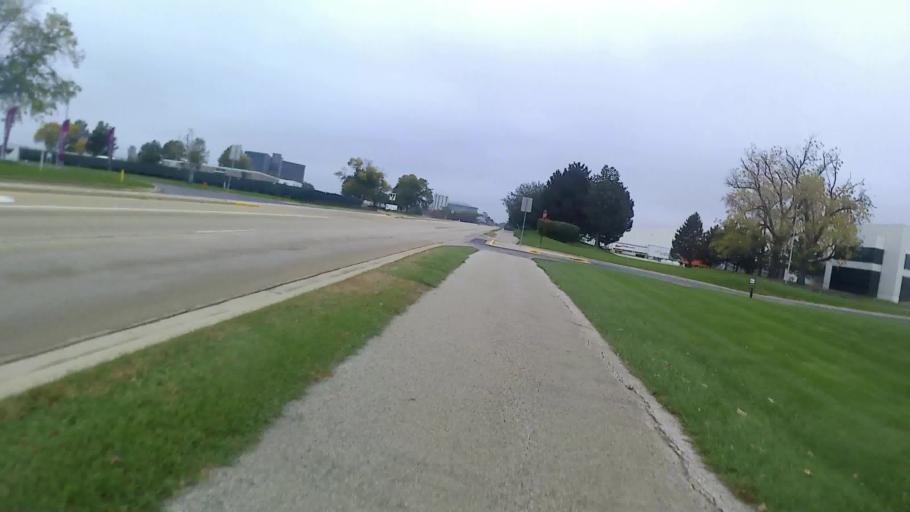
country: US
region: Illinois
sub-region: DuPage County
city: Warrenville
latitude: 41.8075
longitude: -88.1902
